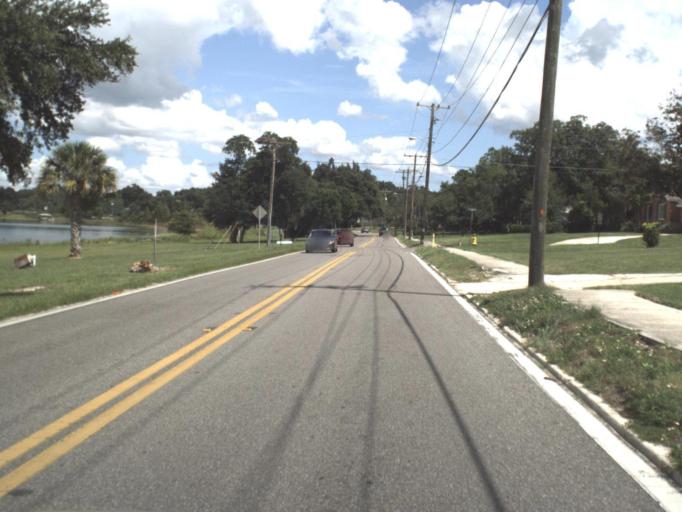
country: US
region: Florida
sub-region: Polk County
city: Winter Haven
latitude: 28.0224
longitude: -81.7121
